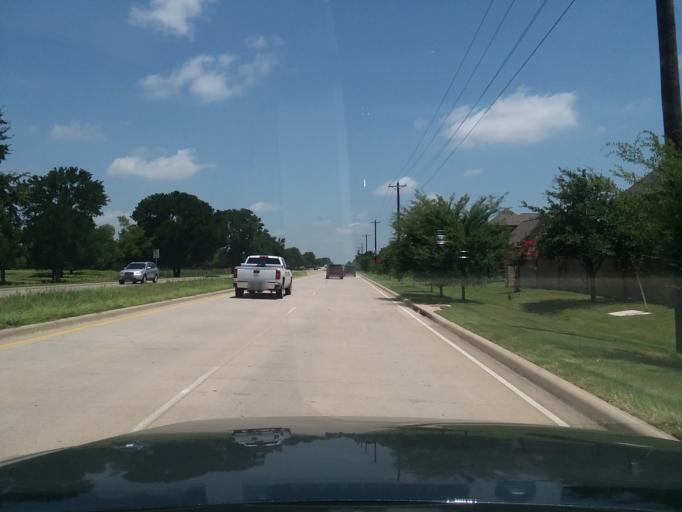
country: US
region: Texas
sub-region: Denton County
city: Bartonville
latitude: 33.0817
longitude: -97.1312
